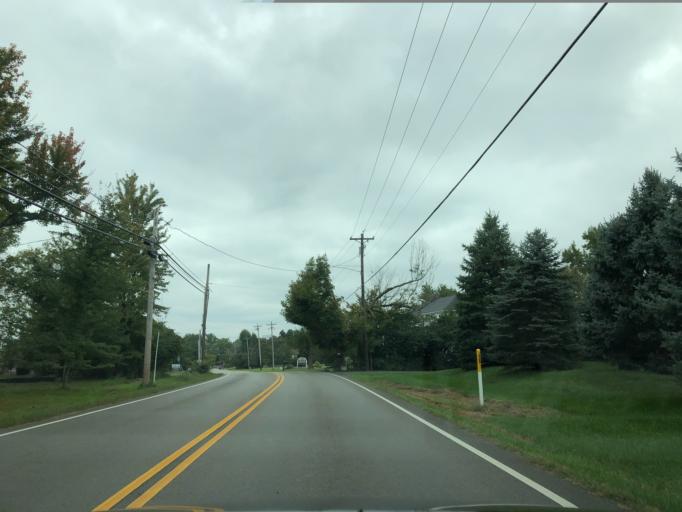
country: US
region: Ohio
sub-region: Warren County
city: Loveland Park
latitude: 39.2888
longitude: -84.2828
